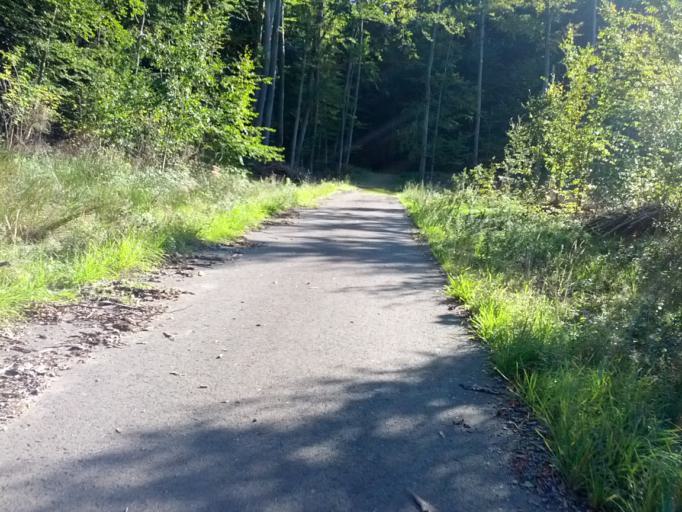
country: DE
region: Thuringia
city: Krauthausen
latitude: 51.0097
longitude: 10.2898
